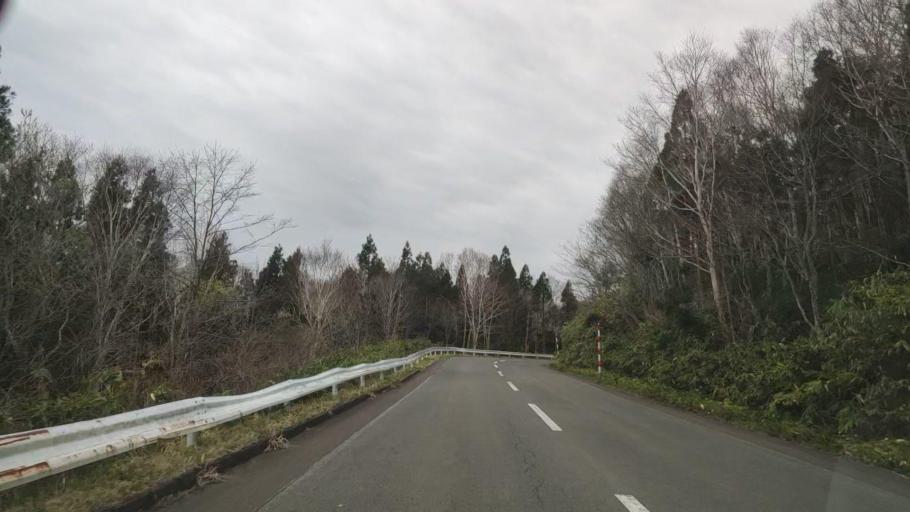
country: JP
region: Akita
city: Hanawa
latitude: 40.4161
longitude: 140.8434
